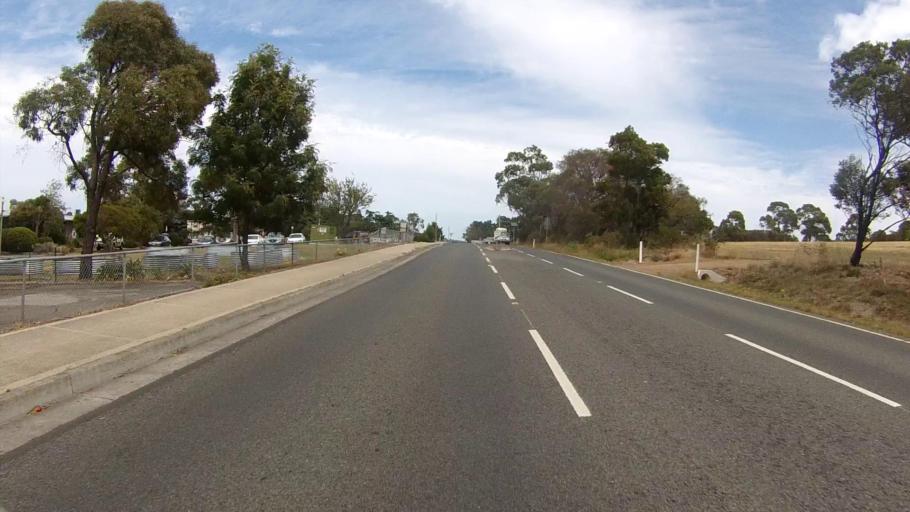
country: AU
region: Tasmania
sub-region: Clarence
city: Lauderdale
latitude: -42.9036
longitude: 147.4777
